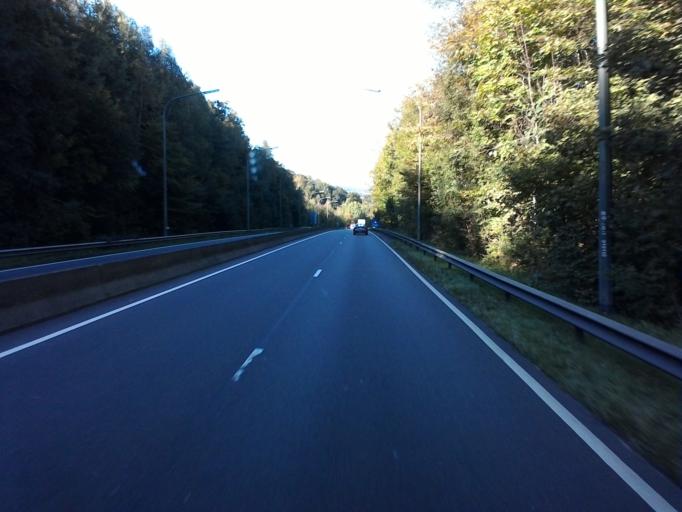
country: BE
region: Wallonia
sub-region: Province du Luxembourg
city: Messancy
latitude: 49.5945
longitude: 5.8080
